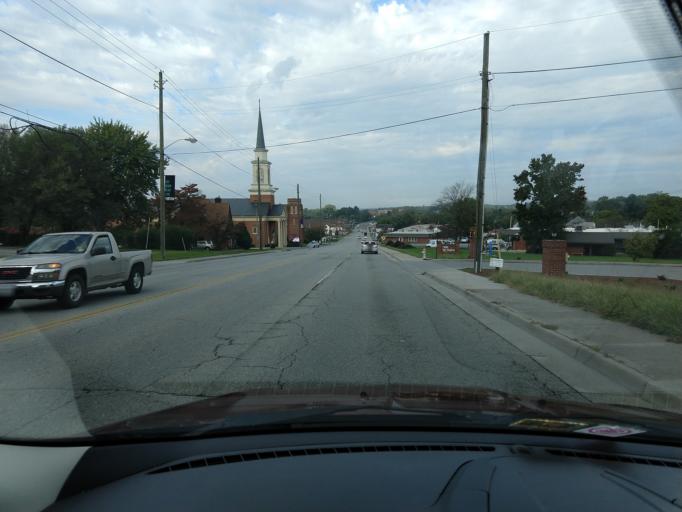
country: US
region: Virginia
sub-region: Roanoke County
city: Vinton
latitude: 37.2807
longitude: -79.8937
